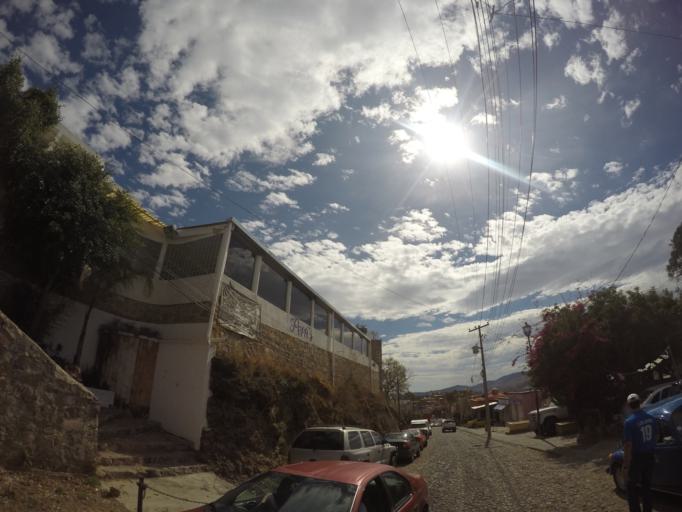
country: MX
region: Guanajuato
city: Guanajuato
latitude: 21.0159
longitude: -101.2598
